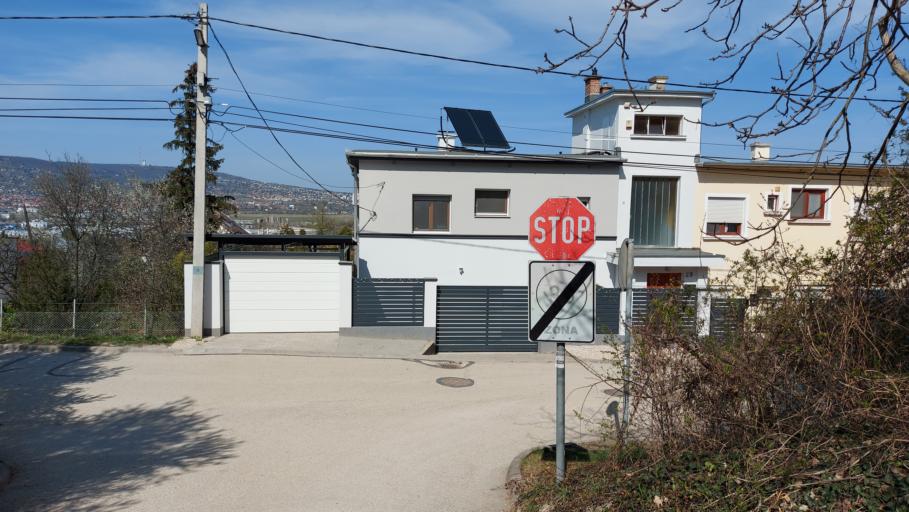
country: HU
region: Pest
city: Budaors
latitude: 47.4333
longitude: 18.9722
